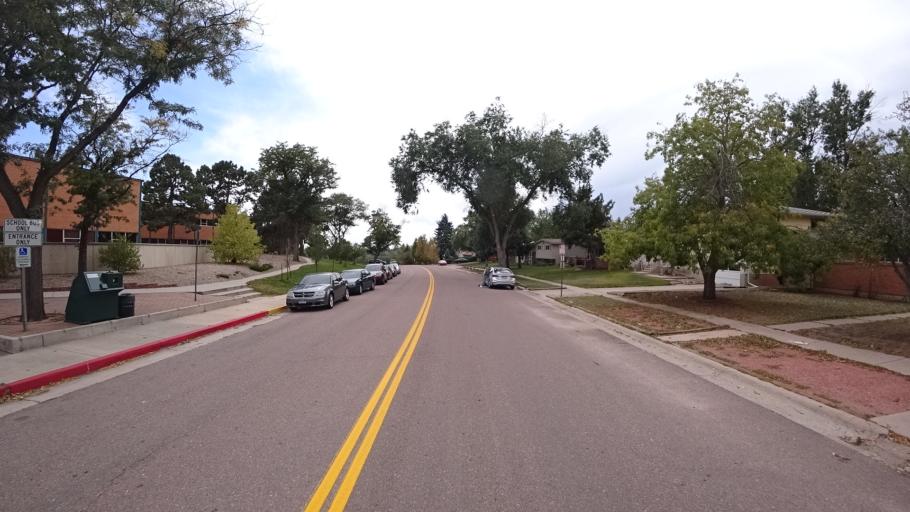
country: US
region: Colorado
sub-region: El Paso County
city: Colorado Springs
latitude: 38.8616
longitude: -104.7838
